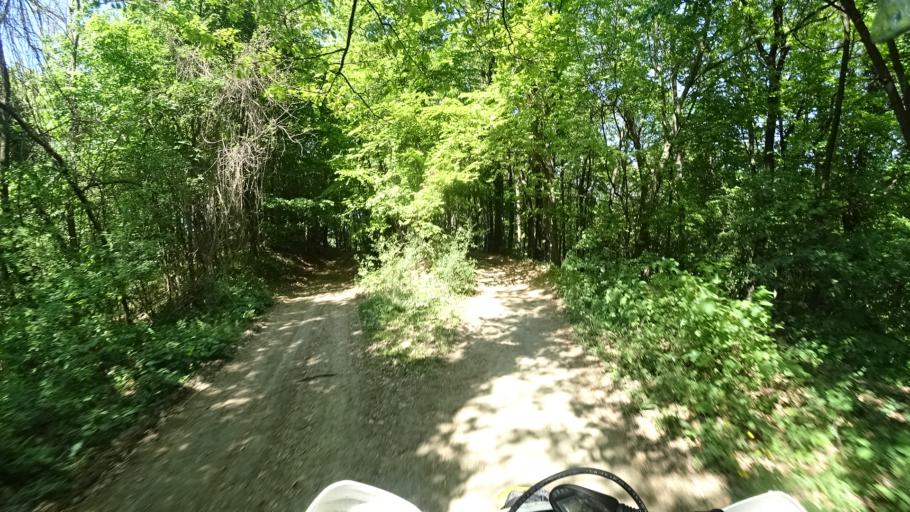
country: HR
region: Zagrebacka
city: Jablanovec
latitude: 45.8663
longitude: 15.8858
